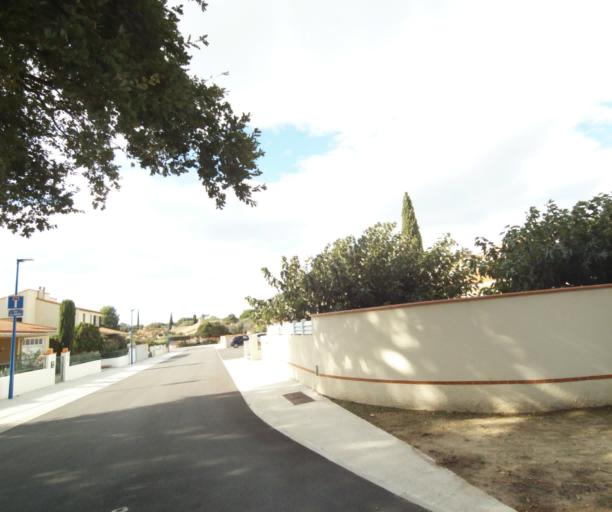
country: FR
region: Languedoc-Roussillon
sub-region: Departement des Pyrenees-Orientales
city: Argelers
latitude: 42.5419
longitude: 3.0164
